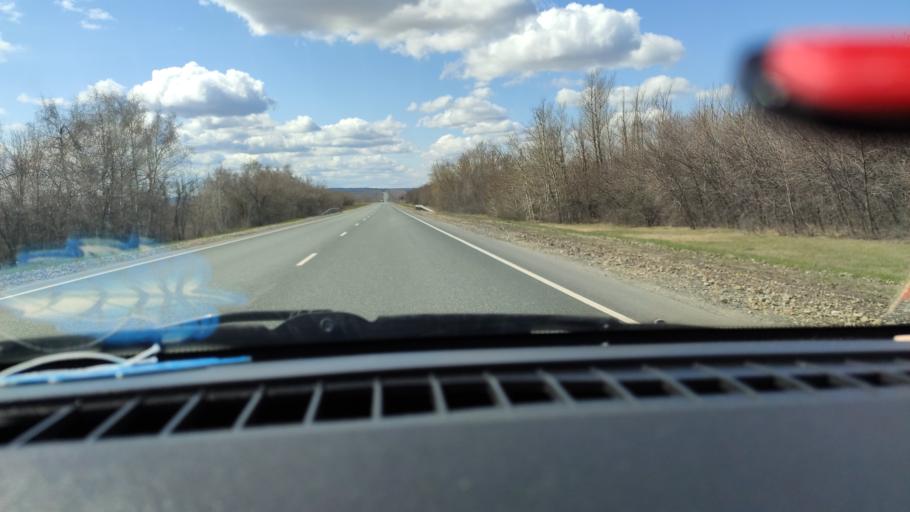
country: RU
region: Saratov
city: Khvalynsk
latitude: 52.5875
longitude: 48.1258
